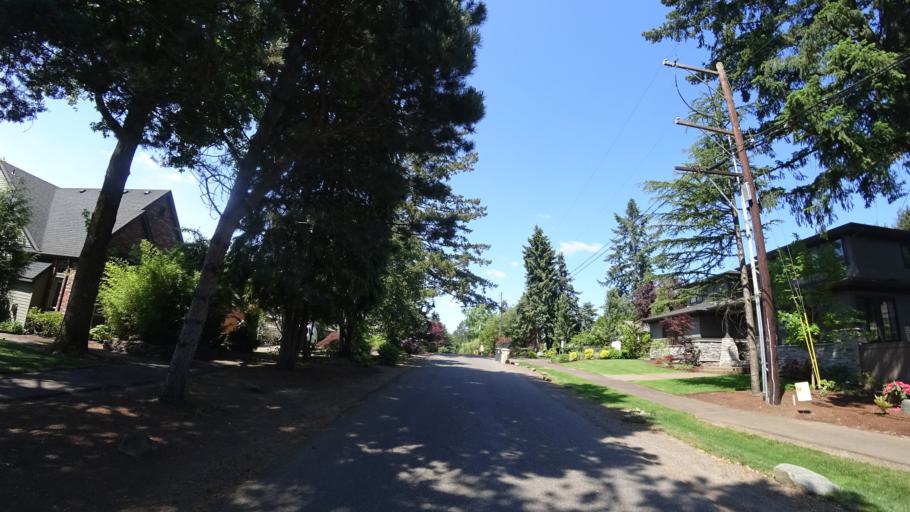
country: US
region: Oregon
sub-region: Clackamas County
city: Lake Oswego
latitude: 45.4324
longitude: -122.7001
